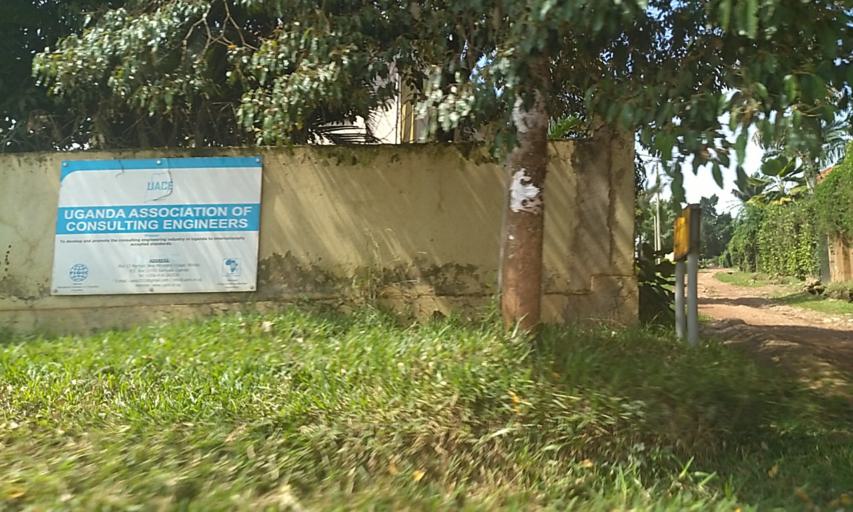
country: UG
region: Central Region
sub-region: Wakiso District
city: Kireka
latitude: 0.3543
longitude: 32.6174
